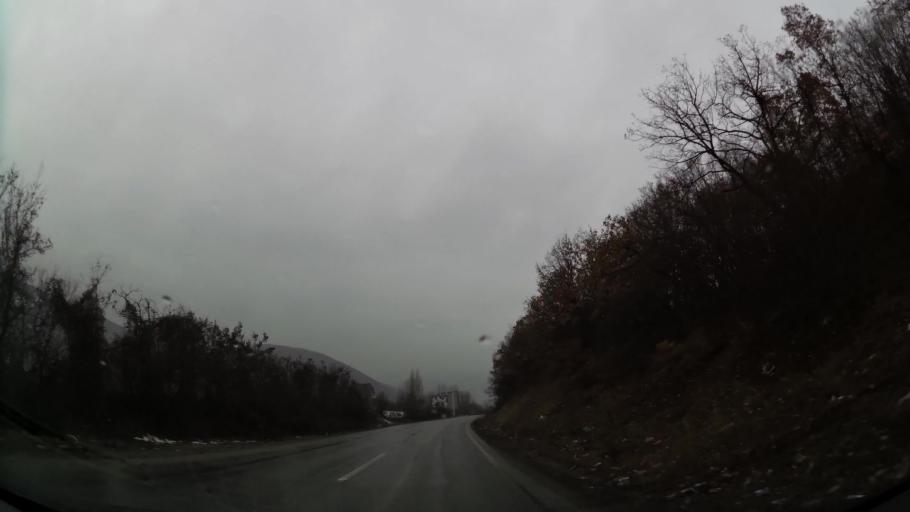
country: XK
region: Ferizaj
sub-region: Hani i Elezit
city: Hani i Elezit
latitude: 42.1335
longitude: 21.3096
